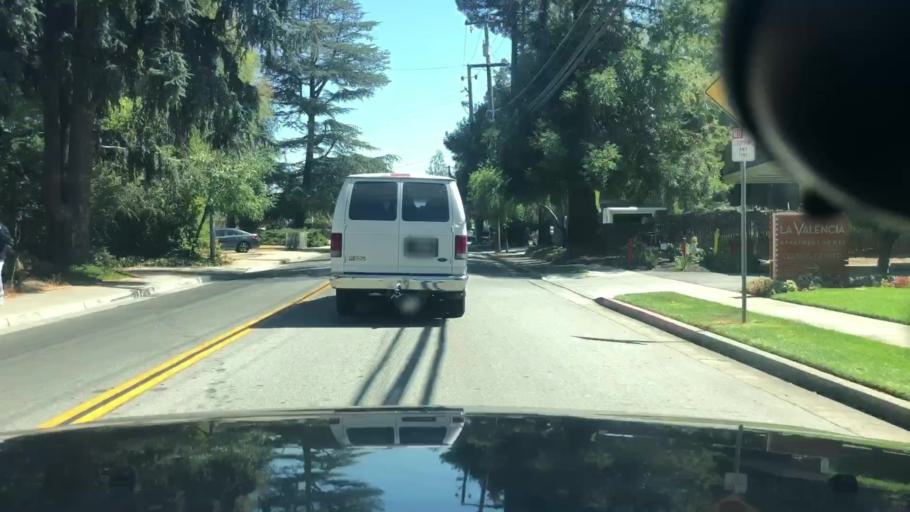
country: US
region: California
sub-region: Santa Clara County
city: Campbell
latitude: 37.2807
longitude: -121.9552
